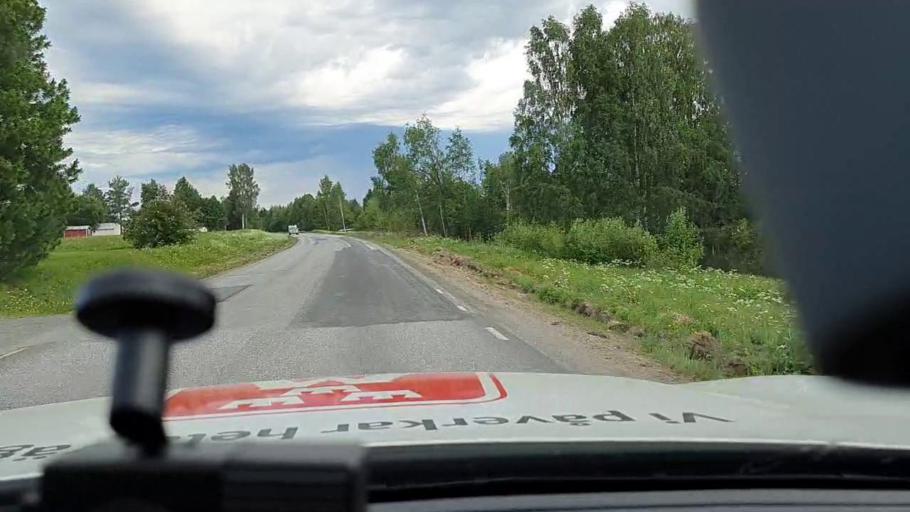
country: SE
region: Norrbotten
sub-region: Bodens Kommun
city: Saevast
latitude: 65.7671
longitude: 21.6905
